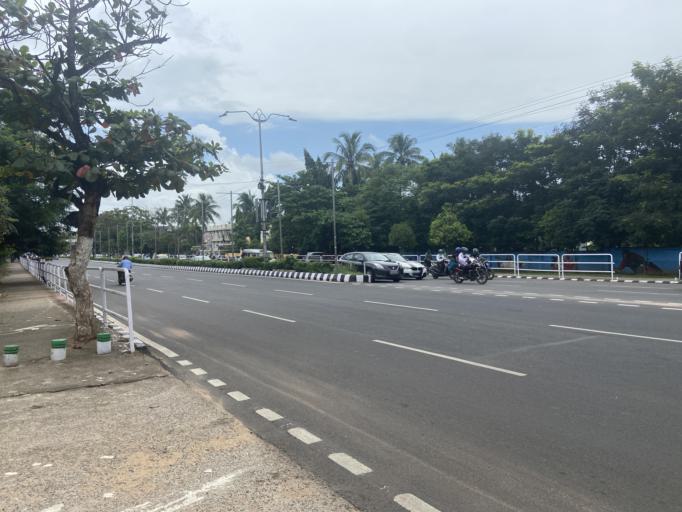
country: IN
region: Odisha
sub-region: Khordha
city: Bhubaneshwar
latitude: 20.2930
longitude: 85.8255
